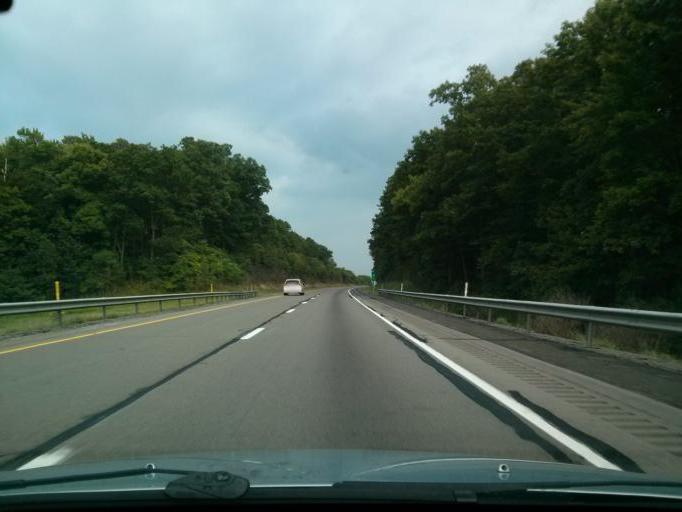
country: US
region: Pennsylvania
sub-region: Jefferson County
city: Brookville
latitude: 41.1771
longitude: -79.1219
